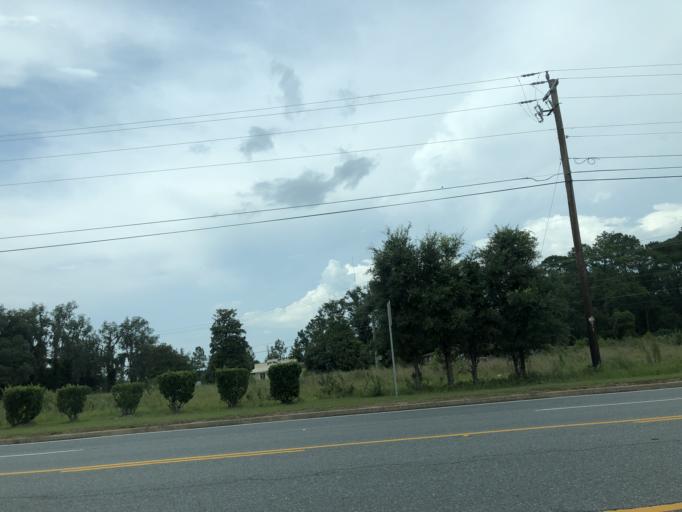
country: US
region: Georgia
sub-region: Wayne County
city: Jesup
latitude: 31.6182
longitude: -81.8965
